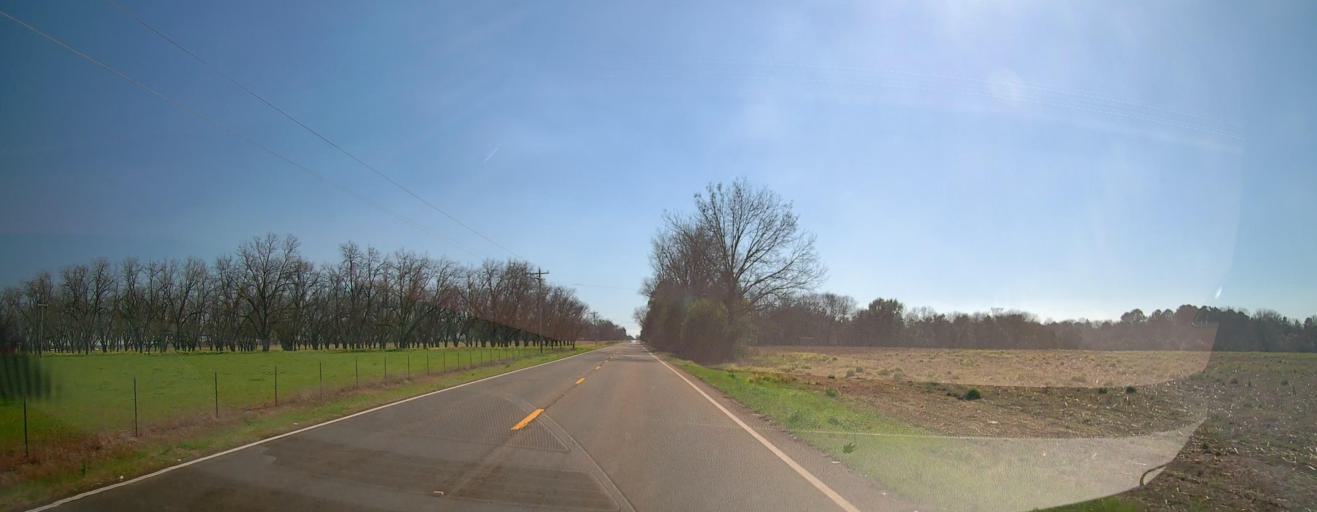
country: US
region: Georgia
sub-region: Macon County
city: Montezuma
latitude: 32.3420
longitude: -84.0200
